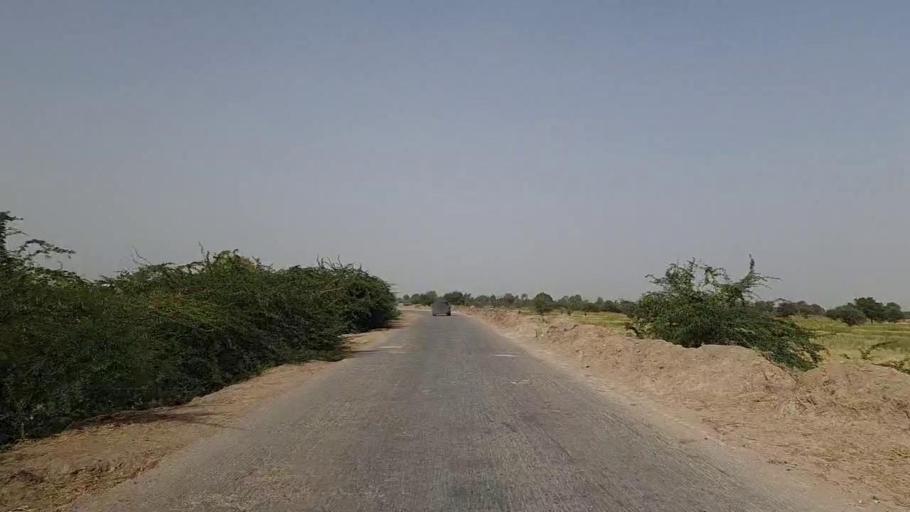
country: PK
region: Sindh
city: Tando Bago
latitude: 24.8930
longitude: 69.0779
